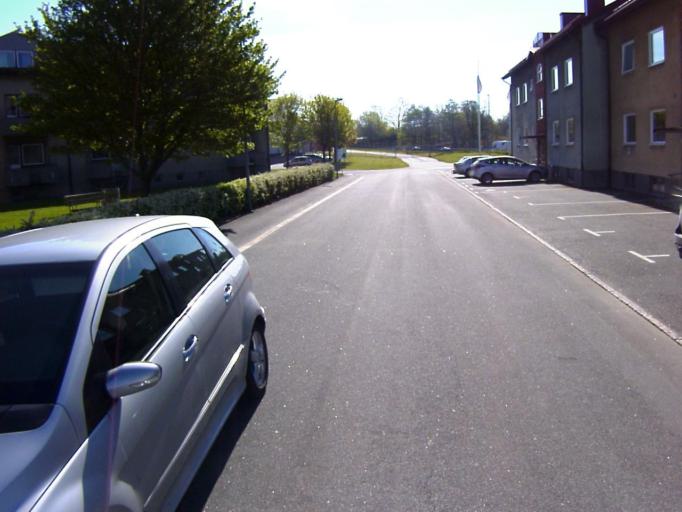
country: SE
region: Skane
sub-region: Kristianstads Kommun
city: Onnestad
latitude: 55.9311
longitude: 13.9798
